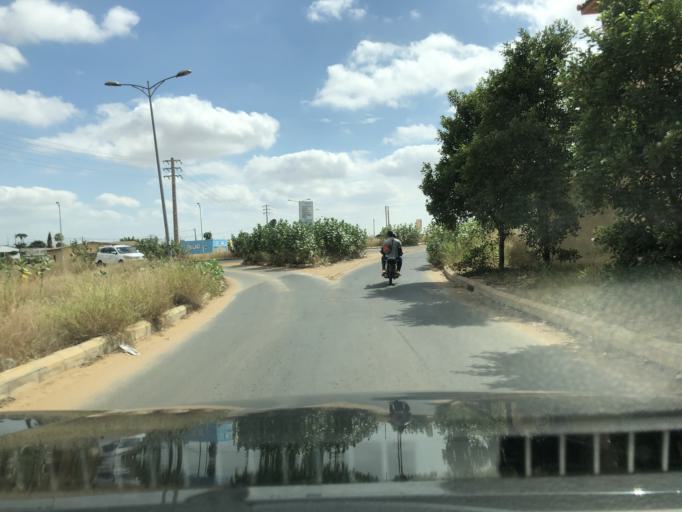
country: AO
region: Luanda
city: Luanda
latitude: -8.9462
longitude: 13.2427
